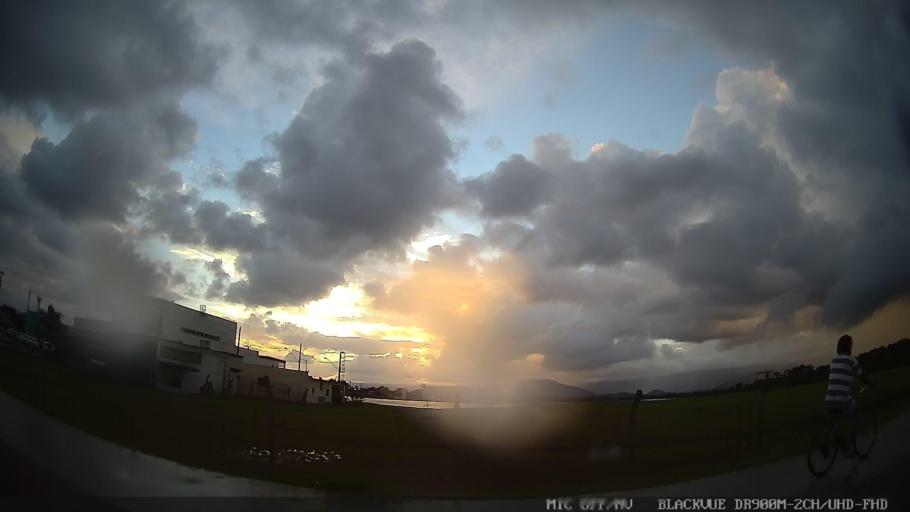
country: BR
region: Sao Paulo
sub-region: Itanhaem
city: Itanhaem
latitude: -24.1655
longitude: -46.7840
